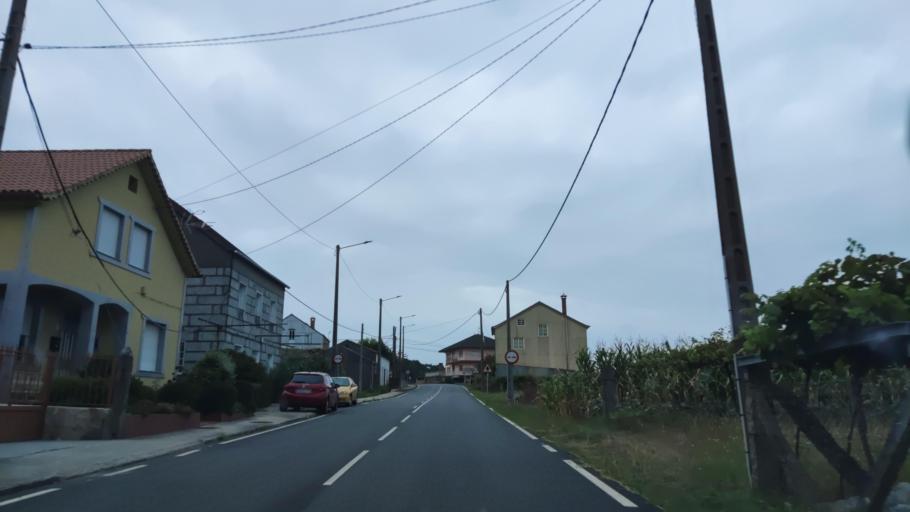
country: ES
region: Galicia
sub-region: Provincia de Pontevedra
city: Catoira
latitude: 42.6682
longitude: -8.7432
